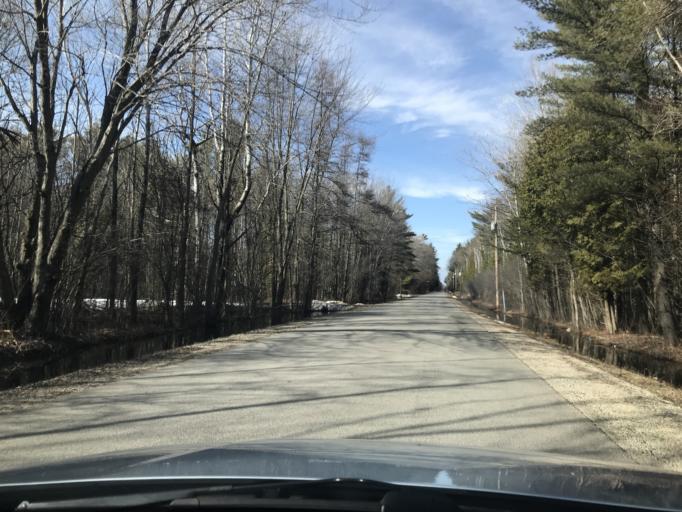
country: US
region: Wisconsin
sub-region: Marinette County
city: Marinette
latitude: 45.0266
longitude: -87.6675
